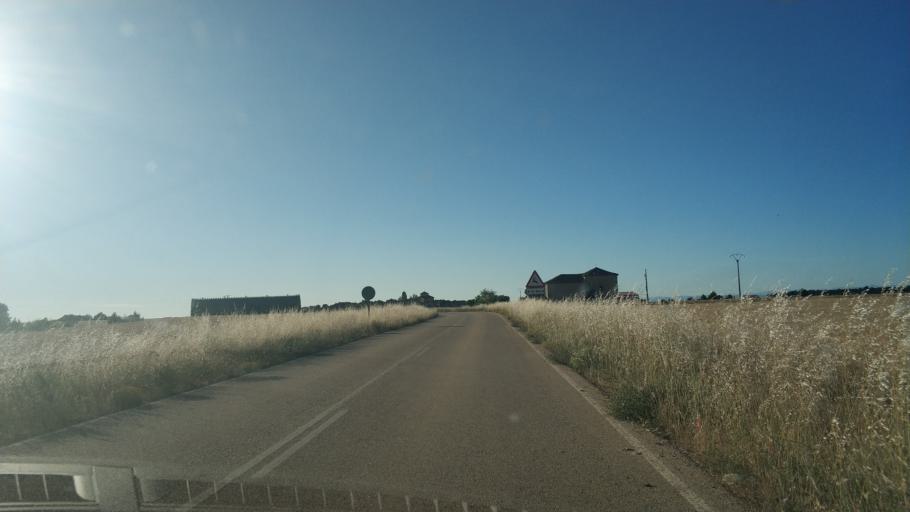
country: ES
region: Castille and Leon
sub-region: Provincia de Soria
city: Liceras
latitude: 41.4592
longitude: -3.2118
